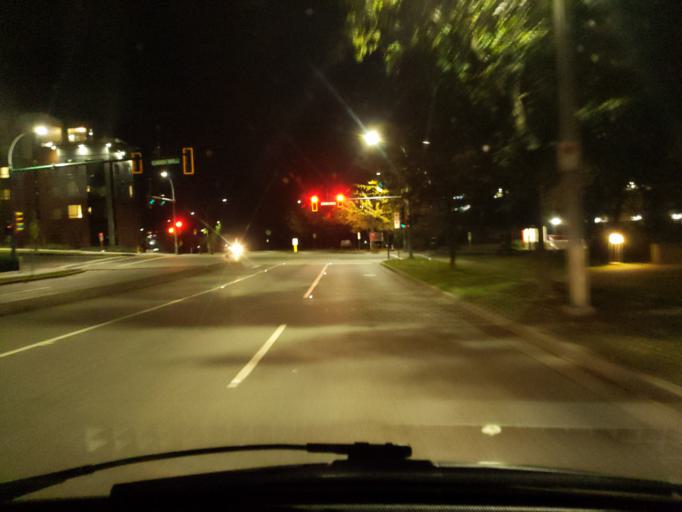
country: CA
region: British Columbia
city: Burnaby
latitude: 49.2541
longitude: -123.0106
